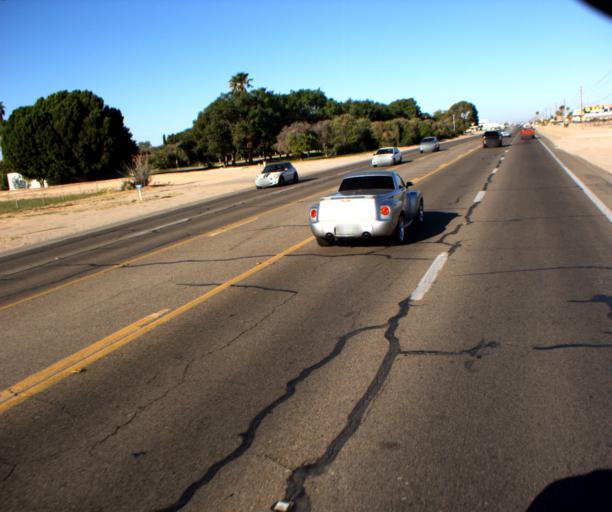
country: US
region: Arizona
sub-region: Yuma County
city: Yuma
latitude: 32.6700
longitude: -114.5506
